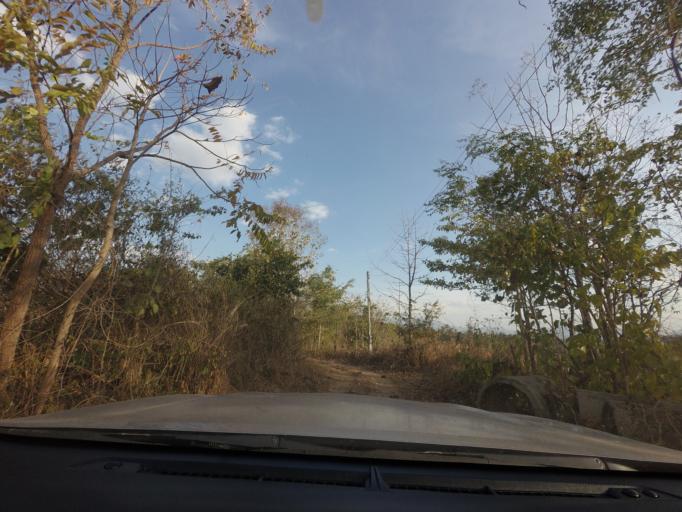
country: TH
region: Mae Hong Son
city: Mae Hi
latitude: 19.3401
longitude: 98.4278
